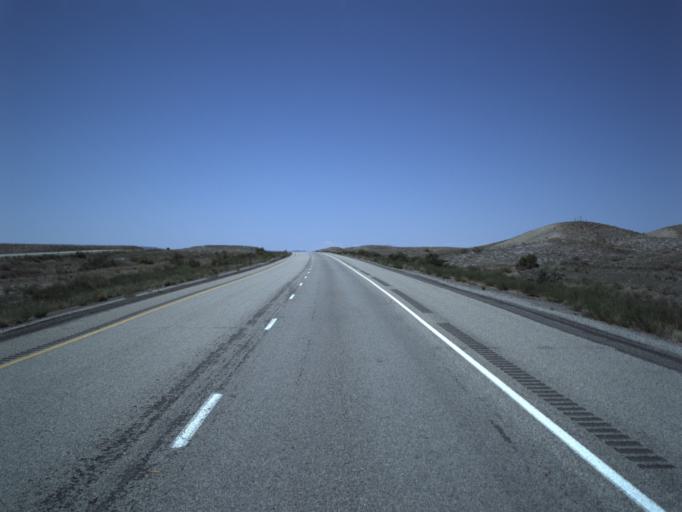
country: US
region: Utah
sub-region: Grand County
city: Moab
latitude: 38.9970
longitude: -109.3262
